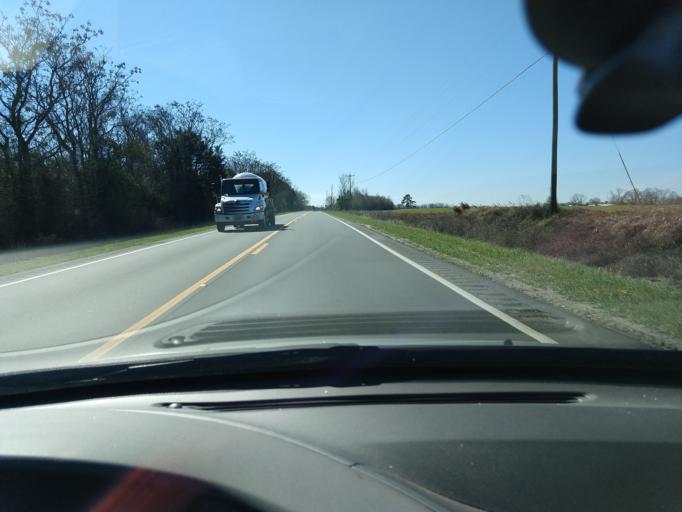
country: US
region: Alabama
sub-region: Covington County
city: Andalusia
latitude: 31.2480
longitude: -86.5252
